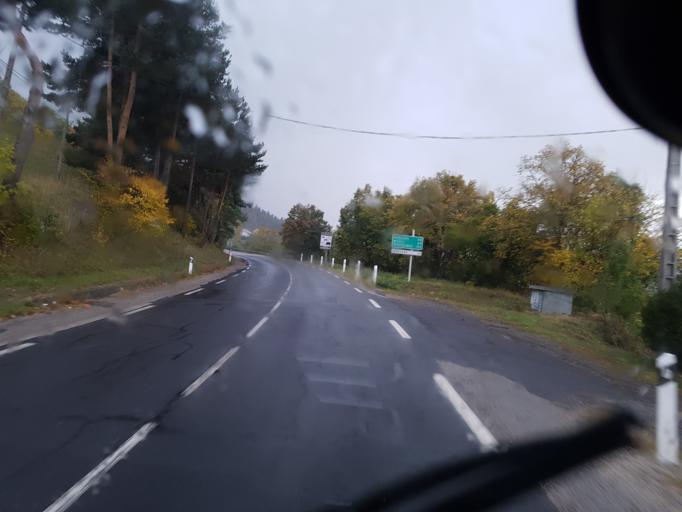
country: FR
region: Auvergne
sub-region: Departement de la Haute-Loire
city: Vals-pres-le-Puy
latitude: 45.0163
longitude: 3.8834
